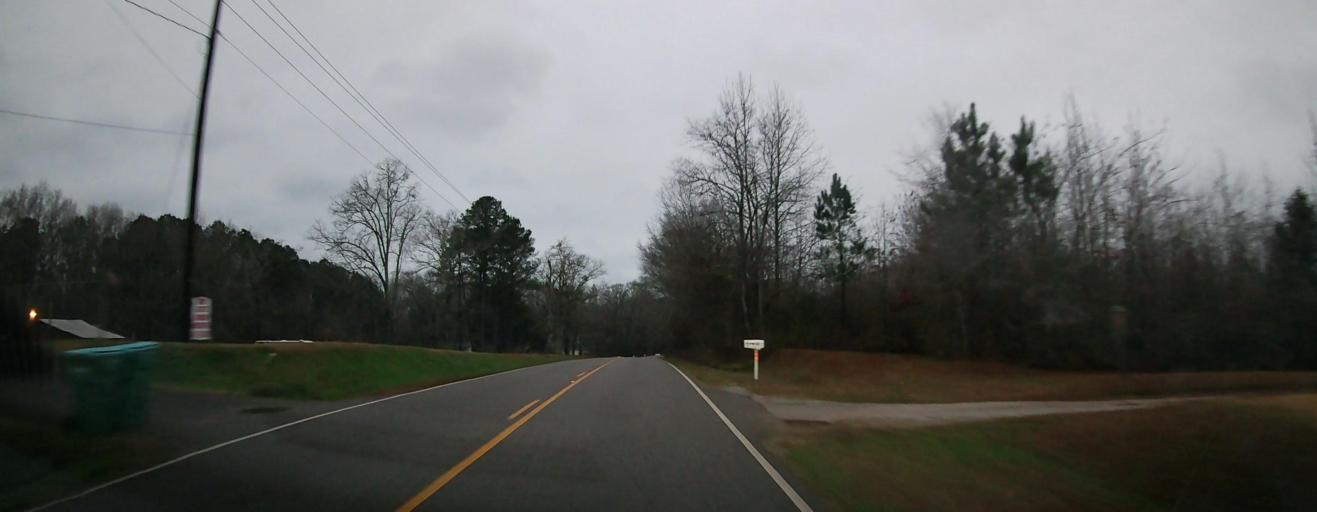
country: US
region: Alabama
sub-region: Tuscaloosa County
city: Vance
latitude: 33.1140
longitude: -87.2177
